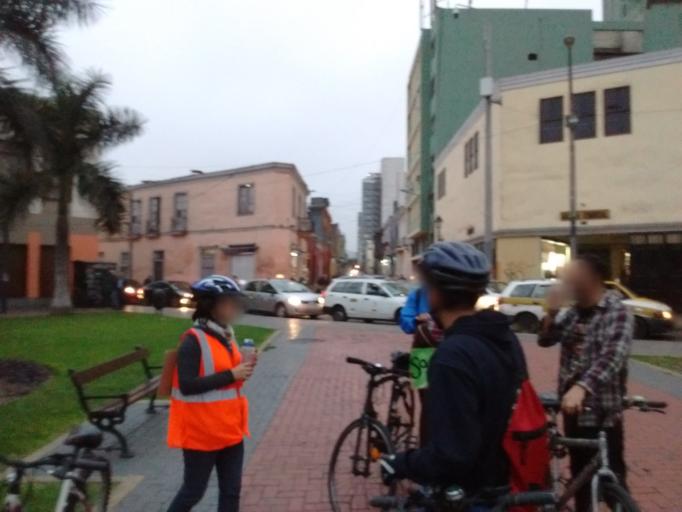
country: PE
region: Lima
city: Lima
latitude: -12.0531
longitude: -77.0377
